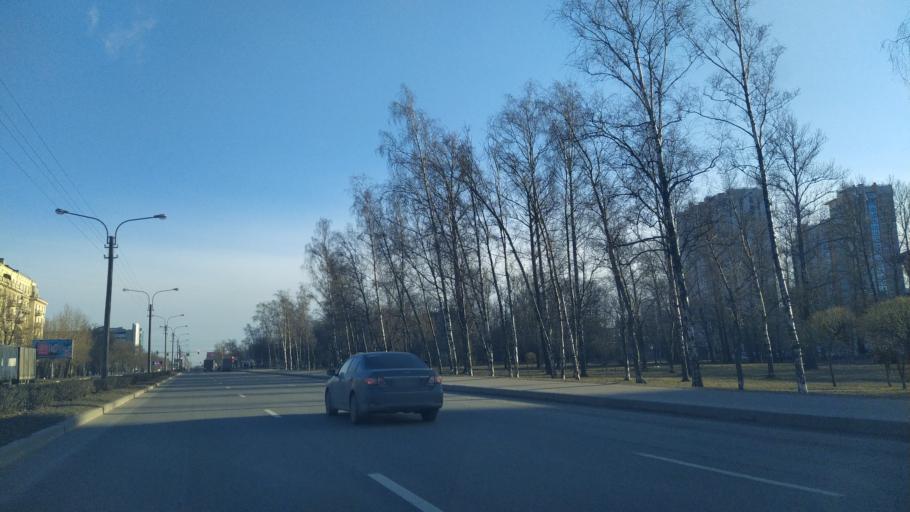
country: RU
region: St.-Petersburg
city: Kupchino
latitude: 59.8355
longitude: 30.3357
